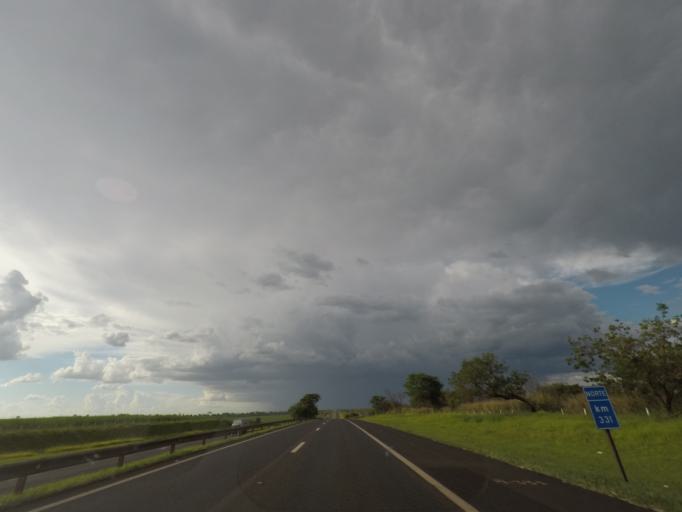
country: BR
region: Sao Paulo
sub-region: Jardinopolis
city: Jardinopolis
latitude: -21.0172
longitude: -47.8418
